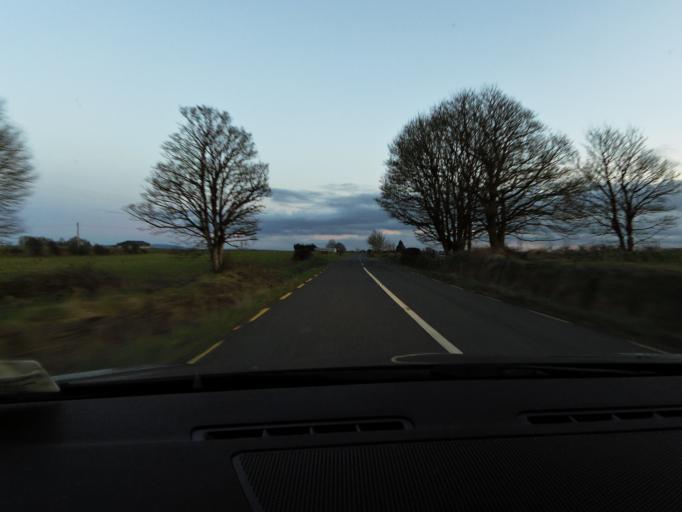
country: IE
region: Connaught
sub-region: Roscommon
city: Boyle
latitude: 53.8468
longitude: -8.2256
